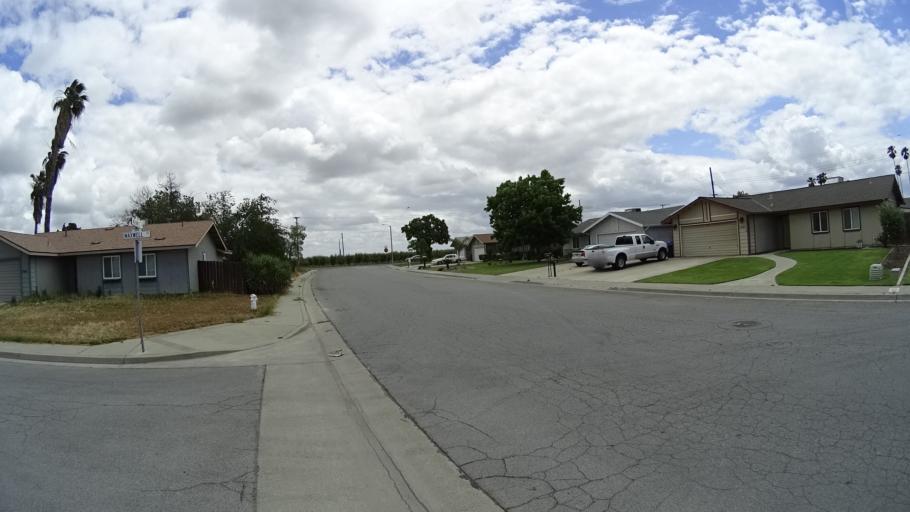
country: US
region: California
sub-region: Kings County
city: Hanford
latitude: 36.3403
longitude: -119.6245
